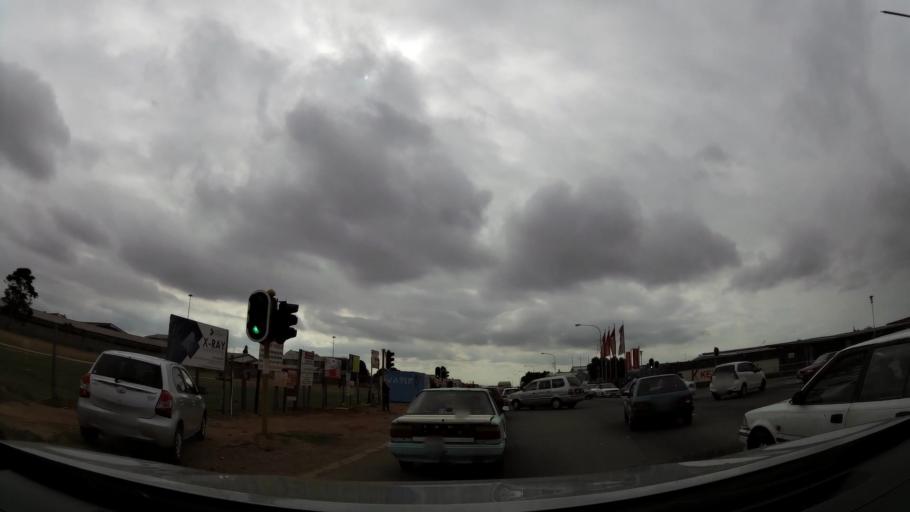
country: ZA
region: Eastern Cape
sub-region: Nelson Mandela Bay Metropolitan Municipality
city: Port Elizabeth
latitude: -33.8835
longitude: 25.5626
